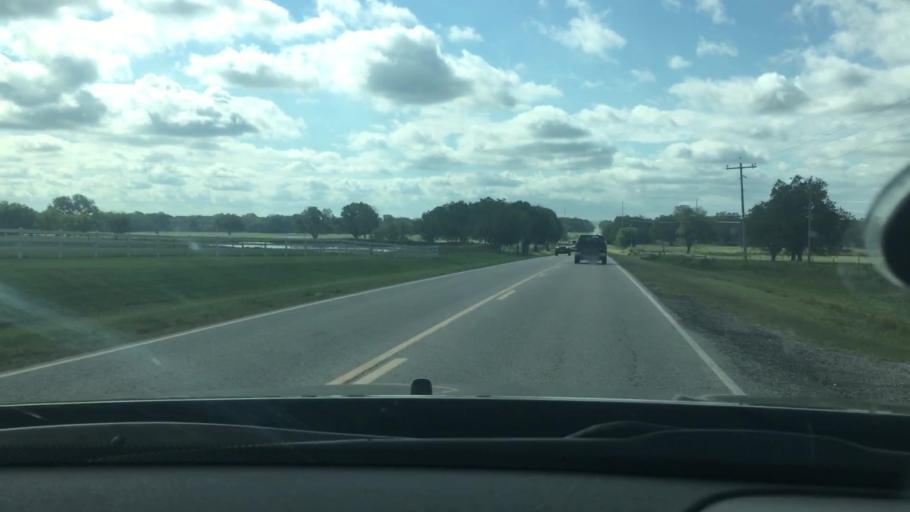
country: US
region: Oklahoma
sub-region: Pontotoc County
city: Ada
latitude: 34.7121
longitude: -96.6349
